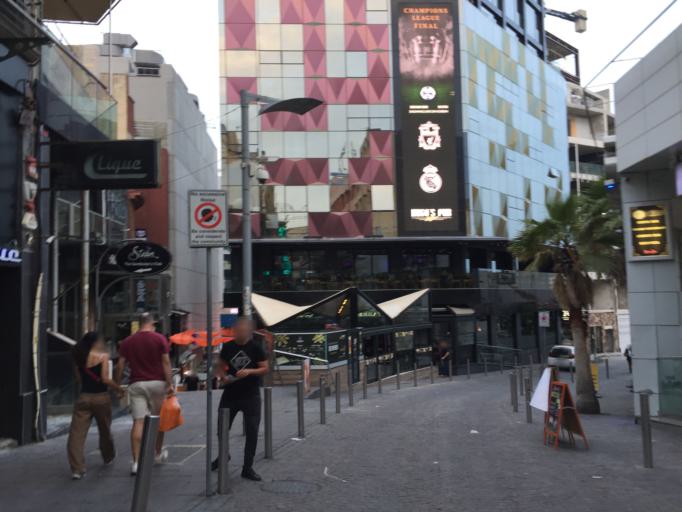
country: MT
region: Saint Julian
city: San Giljan
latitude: 35.9240
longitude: 14.4891
